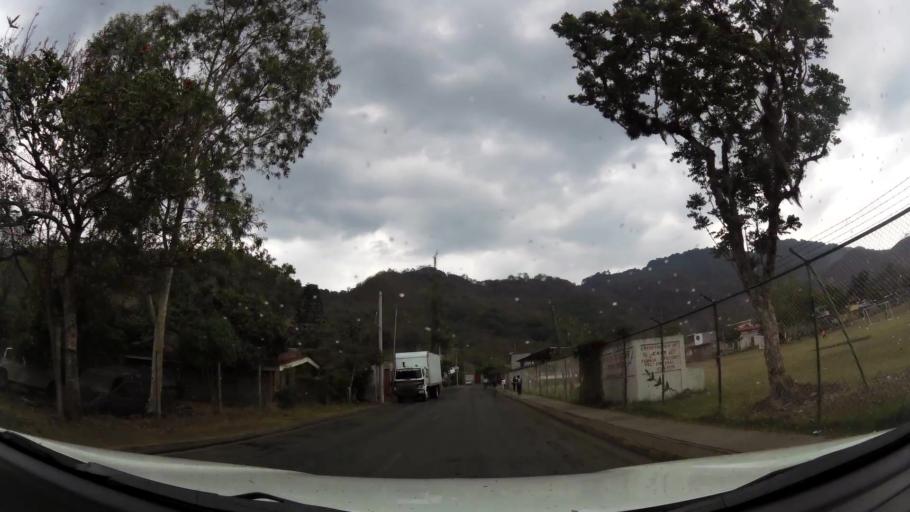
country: NI
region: Jinotega
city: Jinotega
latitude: 13.0896
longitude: -85.9968
